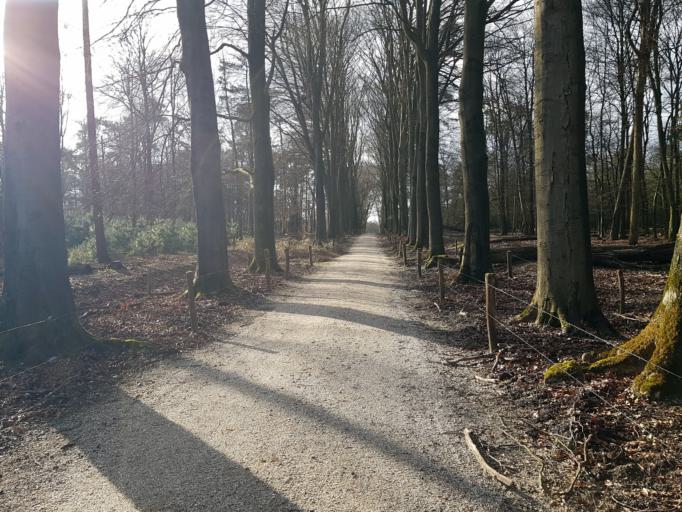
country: NL
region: Gelderland
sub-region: Gemeente Rheden
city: Rheden
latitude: 52.0200
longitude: 6.0109
